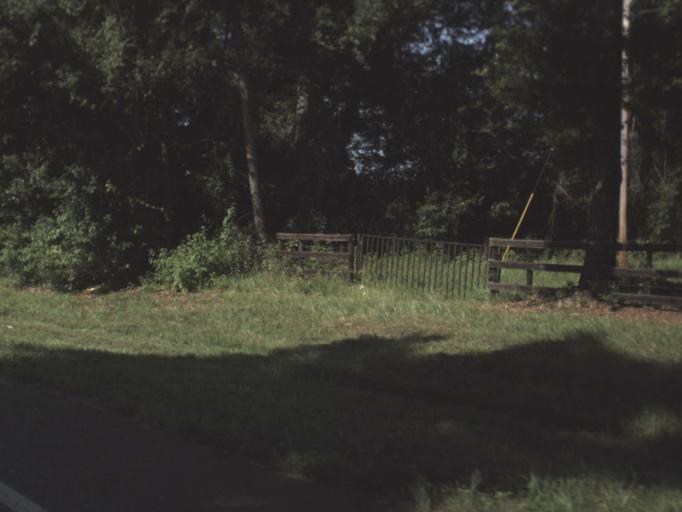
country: US
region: Florida
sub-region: Alachua County
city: High Springs
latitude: 29.9801
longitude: -82.7100
